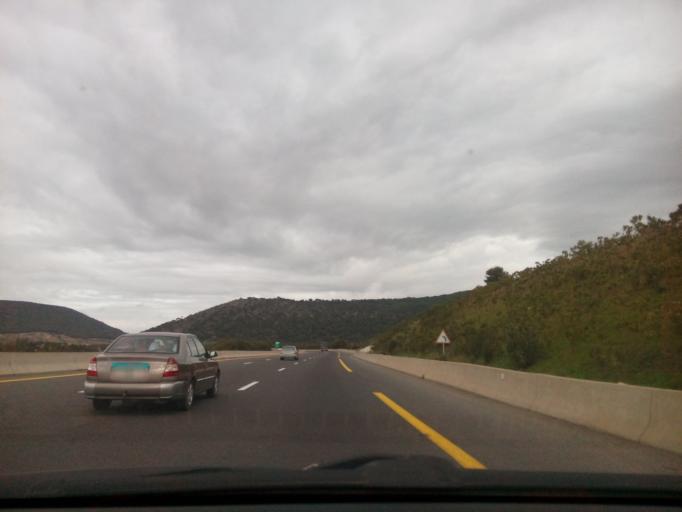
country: DZ
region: Sidi Bel Abbes
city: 'Ain el Berd
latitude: 35.3655
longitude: -0.5034
